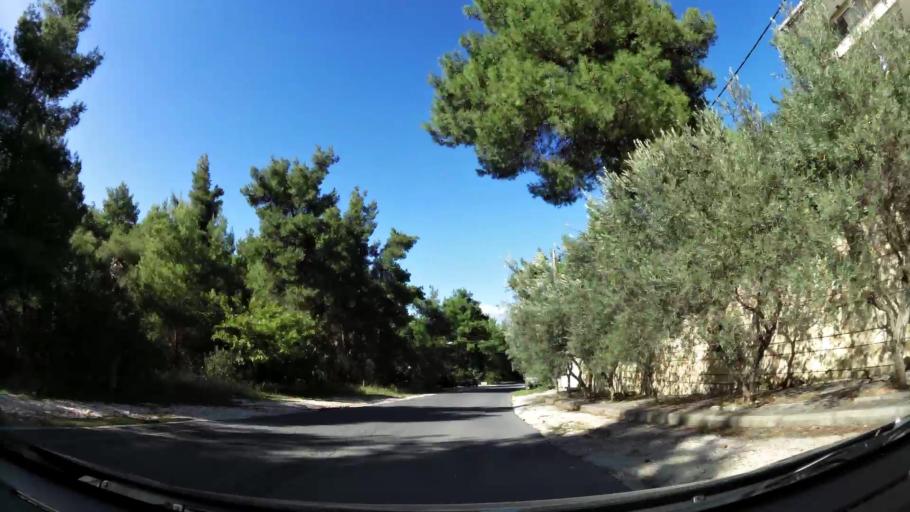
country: GR
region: Attica
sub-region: Nomarchia Anatolikis Attikis
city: Rodopoli
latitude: 38.1105
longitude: 23.8792
